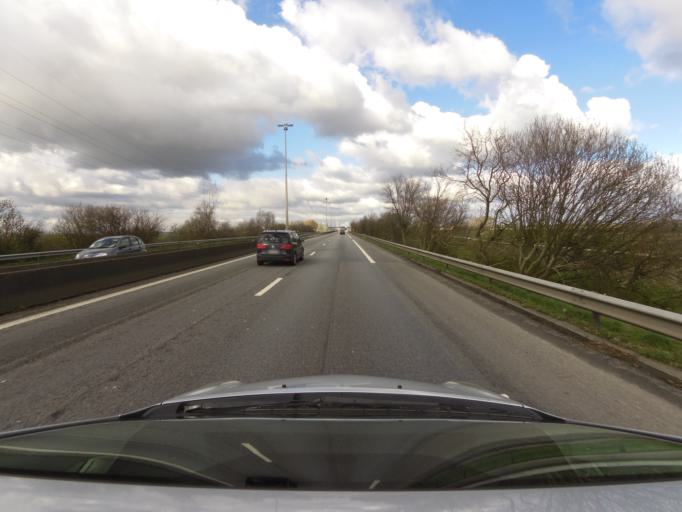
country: FR
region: Nord-Pas-de-Calais
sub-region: Departement du Nord
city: Bourbourg
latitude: 50.9594
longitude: 2.1947
